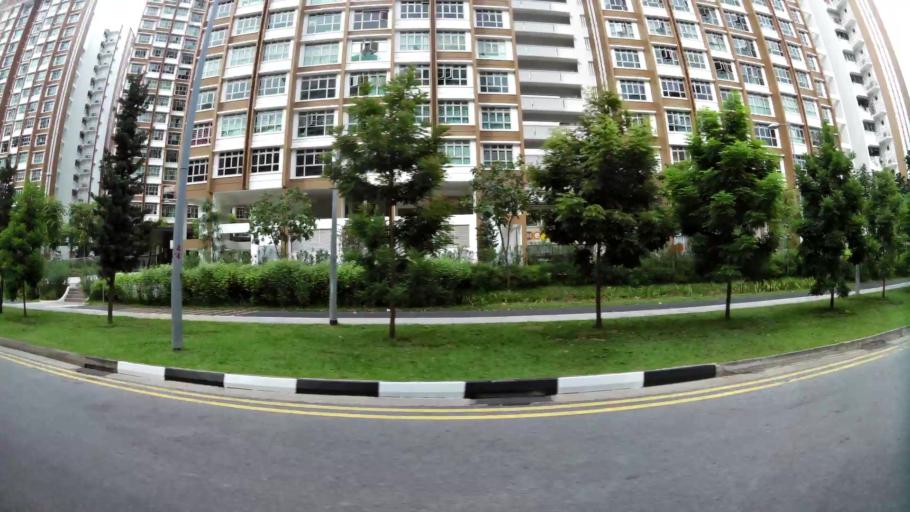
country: MY
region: Johor
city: Kampung Pasir Gudang Baru
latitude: 1.4013
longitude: 103.9145
